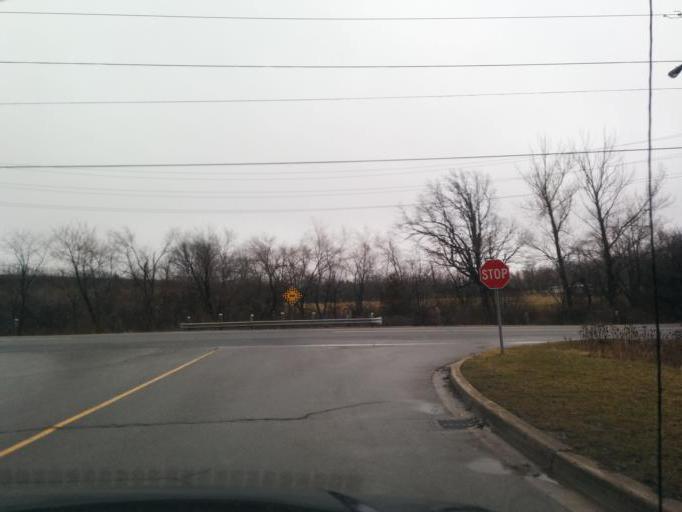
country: CA
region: Ontario
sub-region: Halton
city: Milton
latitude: 43.5158
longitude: -79.9009
